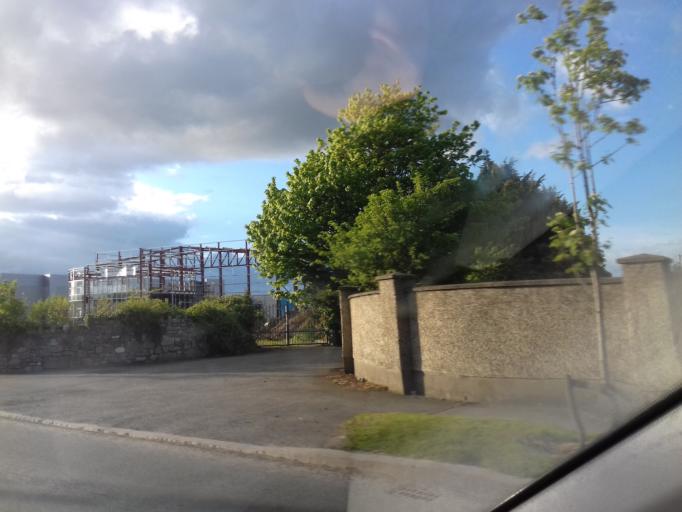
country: IE
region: Leinster
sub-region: South Dublin
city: Rathcoole
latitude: 53.2917
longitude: -6.4712
